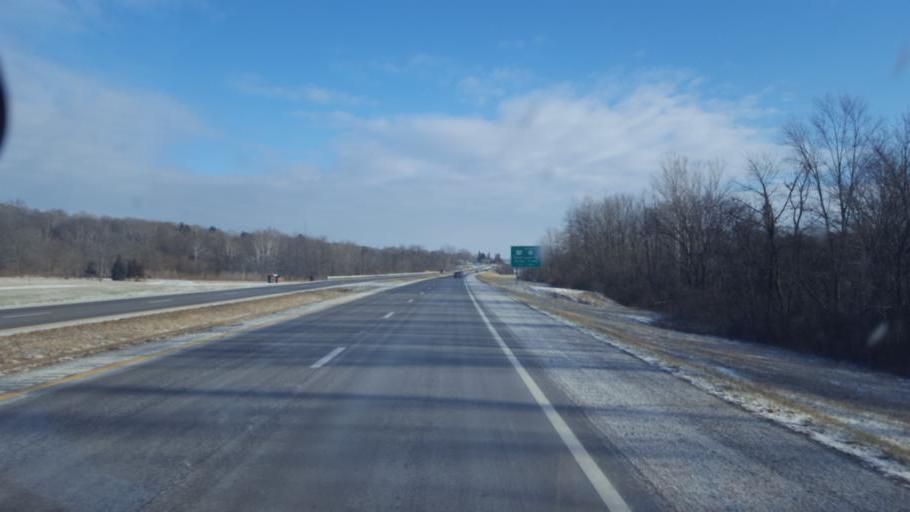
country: US
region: Ohio
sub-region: Ross County
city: Chillicothe
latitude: 39.2764
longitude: -82.9598
